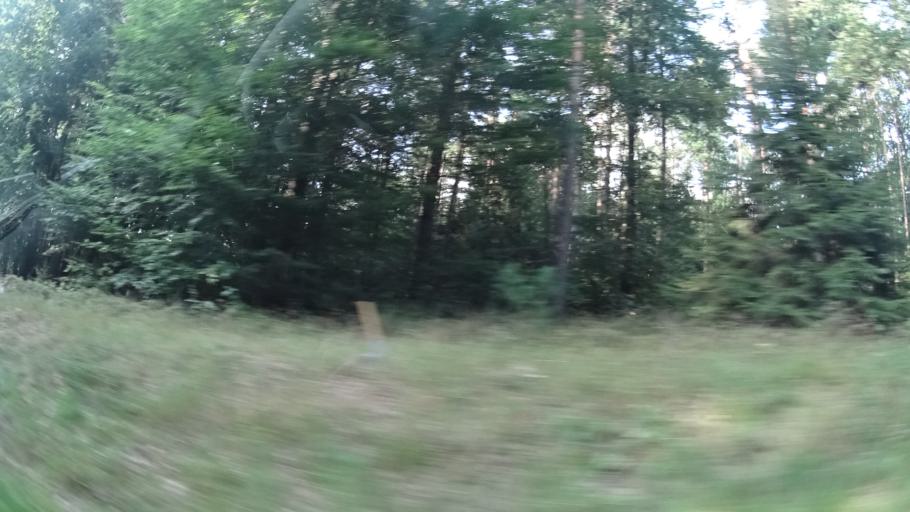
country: DE
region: Hesse
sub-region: Regierungsbezirk Darmstadt
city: Beerfelden
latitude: 49.5498
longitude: 8.9903
